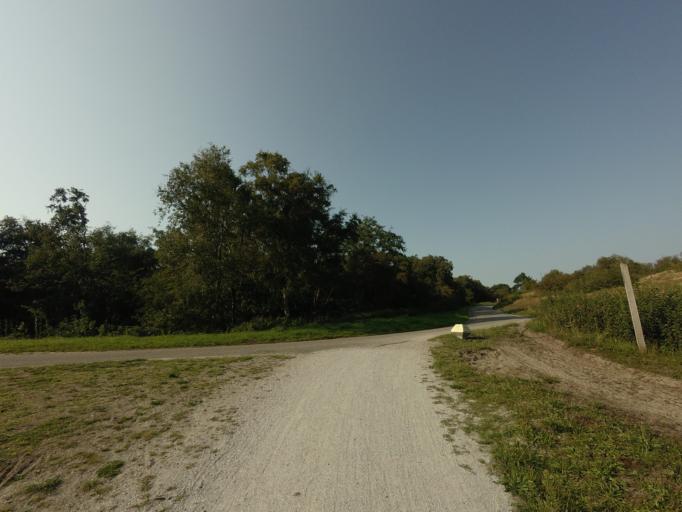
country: NL
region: Friesland
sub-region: Gemeente Schiermonnikoog
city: Schiermonnikoog
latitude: 53.4849
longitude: 6.1788
